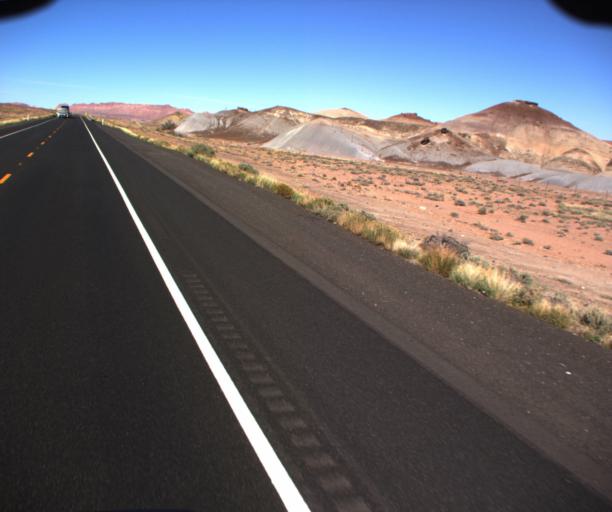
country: US
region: Arizona
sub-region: Coconino County
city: Tuba City
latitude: 36.1305
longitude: -111.3954
